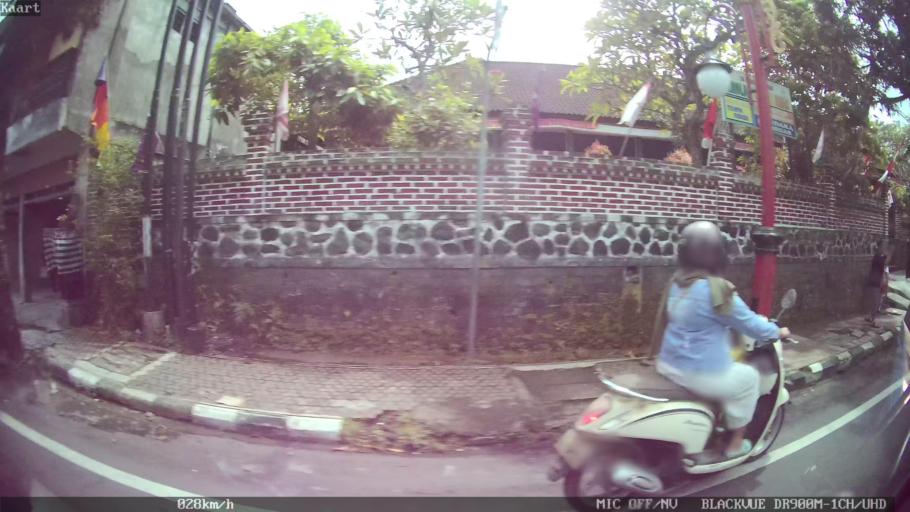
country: ID
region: Bali
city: Banjar Kelodan
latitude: -8.5357
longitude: 115.3280
